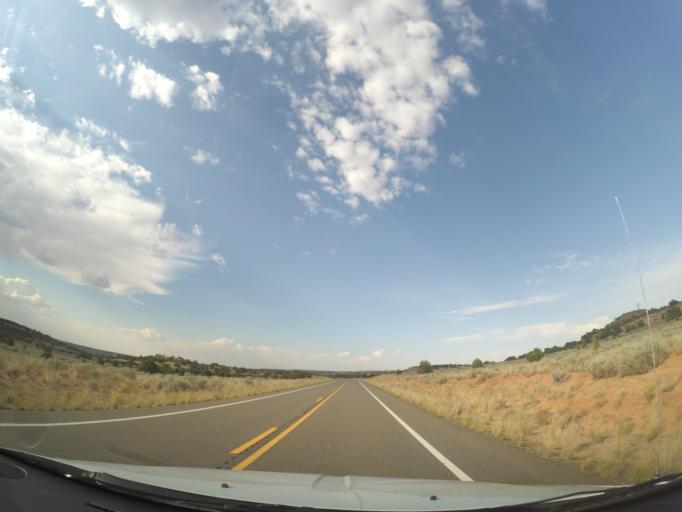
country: US
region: Arizona
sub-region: Coconino County
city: LeChee
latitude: 36.6346
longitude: -111.4425
